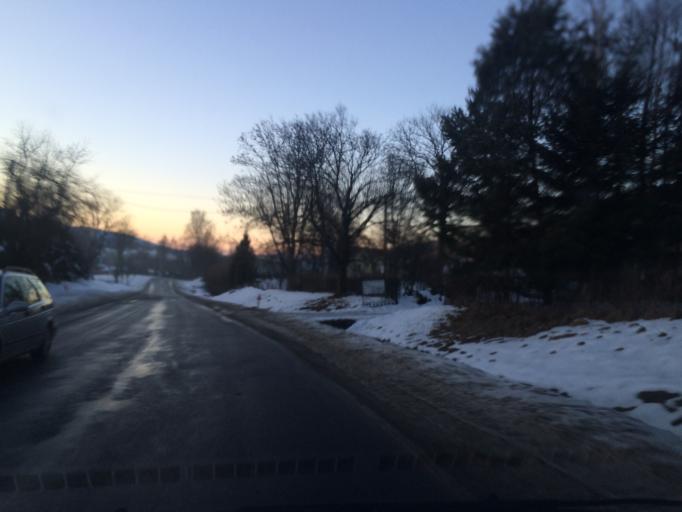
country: PL
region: Subcarpathian Voivodeship
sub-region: Powiat bieszczadzki
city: Czarna
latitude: 49.3568
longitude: 22.6771
